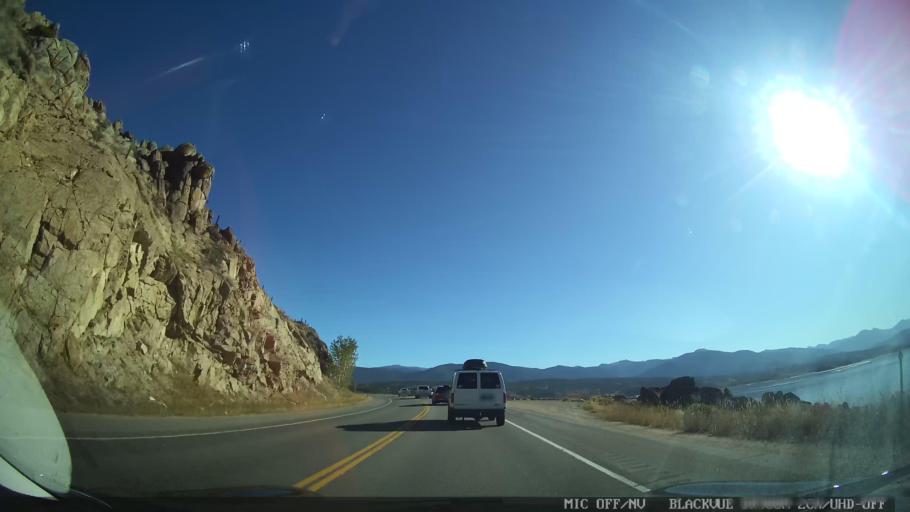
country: US
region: Colorado
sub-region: Grand County
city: Granby
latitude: 40.1837
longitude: -105.8871
